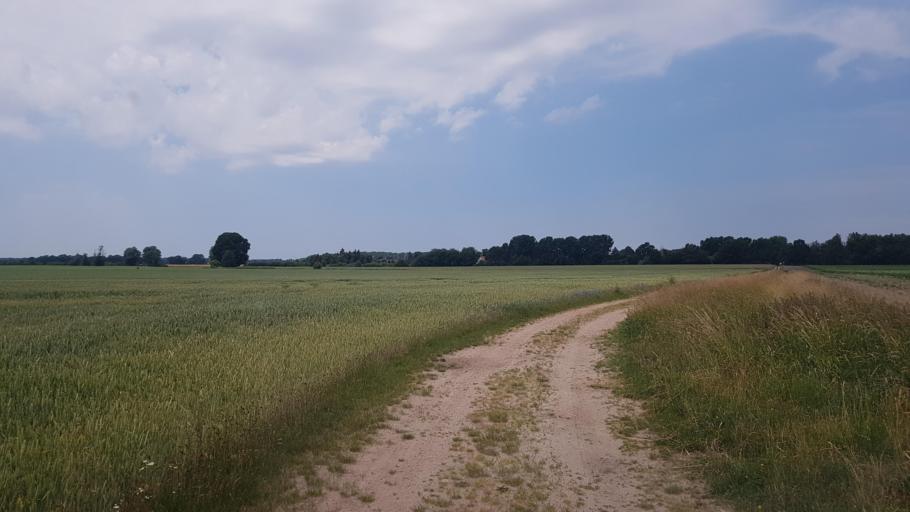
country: DE
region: Brandenburg
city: Finsterwalde
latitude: 51.6820
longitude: 13.7332
